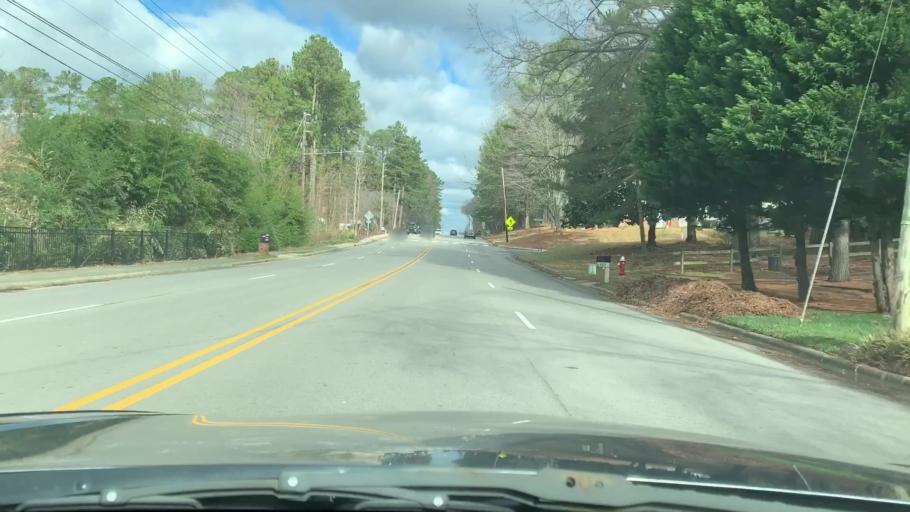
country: US
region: North Carolina
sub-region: Wake County
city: Cary
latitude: 35.7964
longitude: -78.7831
